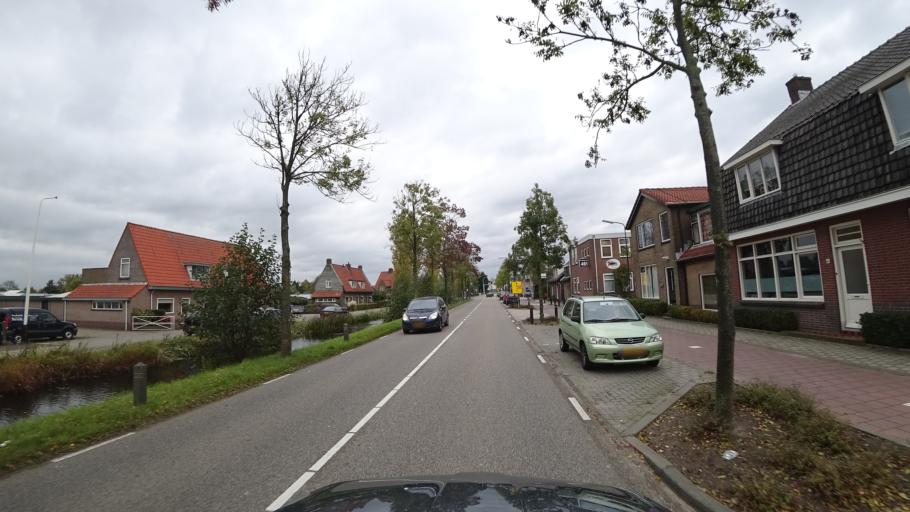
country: NL
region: Utrecht
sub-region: Gemeente Utrecht
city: Utrecht
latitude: 52.1235
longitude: 5.1431
